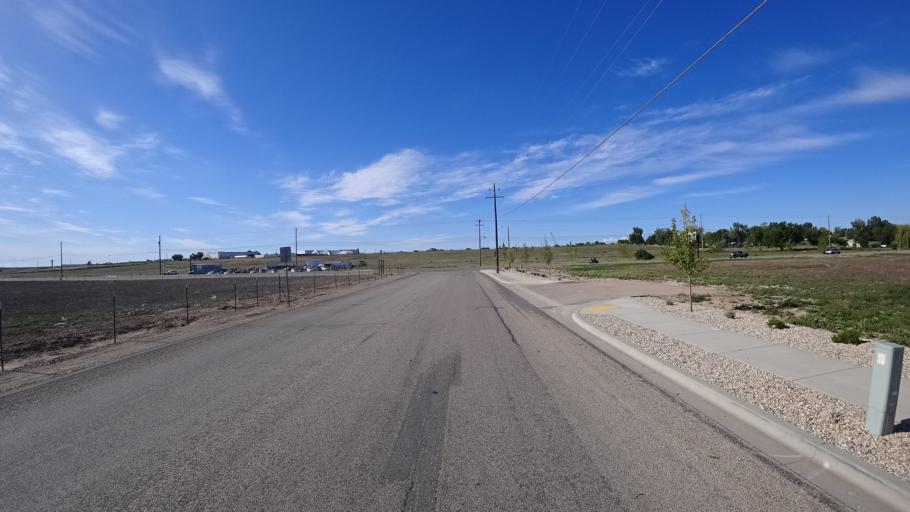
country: US
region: Idaho
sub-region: Ada County
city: Garden City
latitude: 43.5762
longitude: -116.2612
